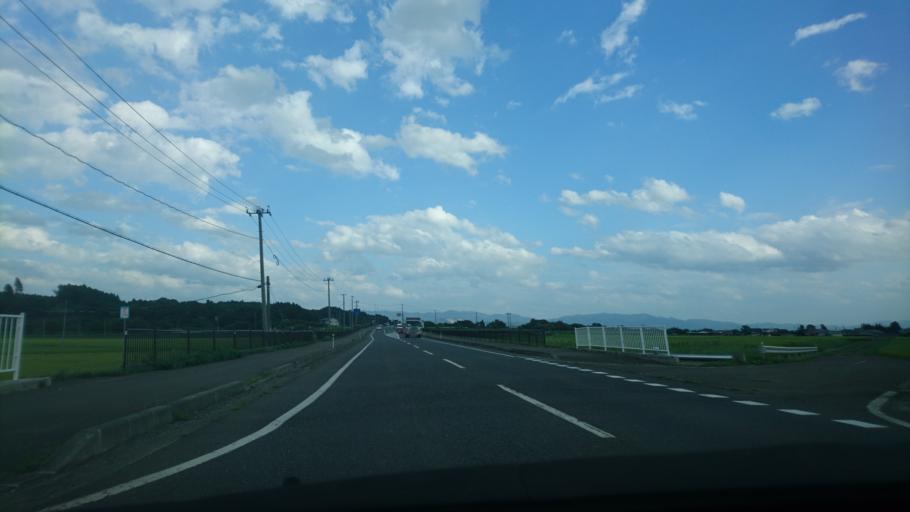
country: JP
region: Iwate
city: Mizusawa
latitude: 39.2076
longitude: 141.1557
